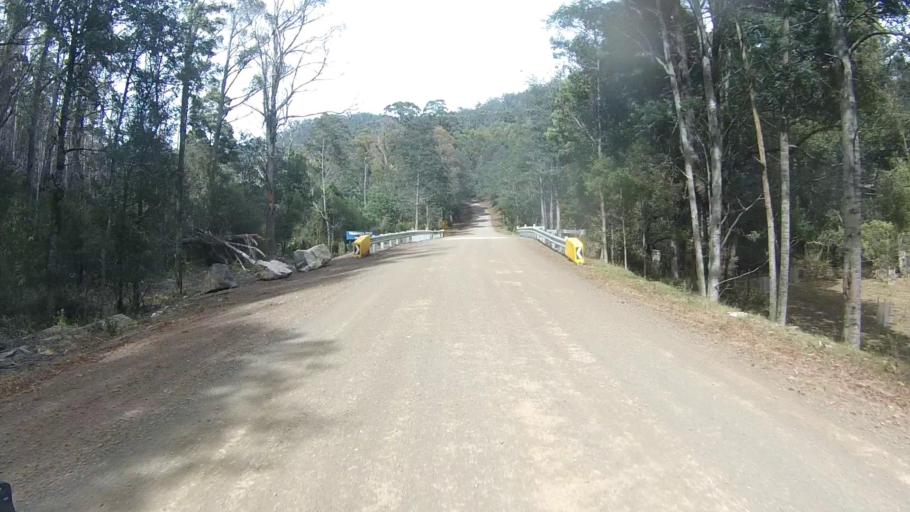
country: AU
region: Tasmania
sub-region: Sorell
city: Sorell
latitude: -42.6924
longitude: 147.8628
